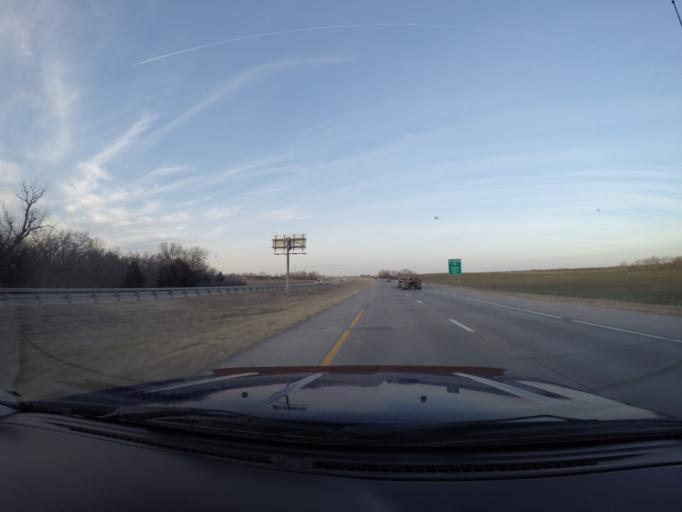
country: US
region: Kansas
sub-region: Saline County
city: Salina
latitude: 38.8562
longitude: -97.6460
